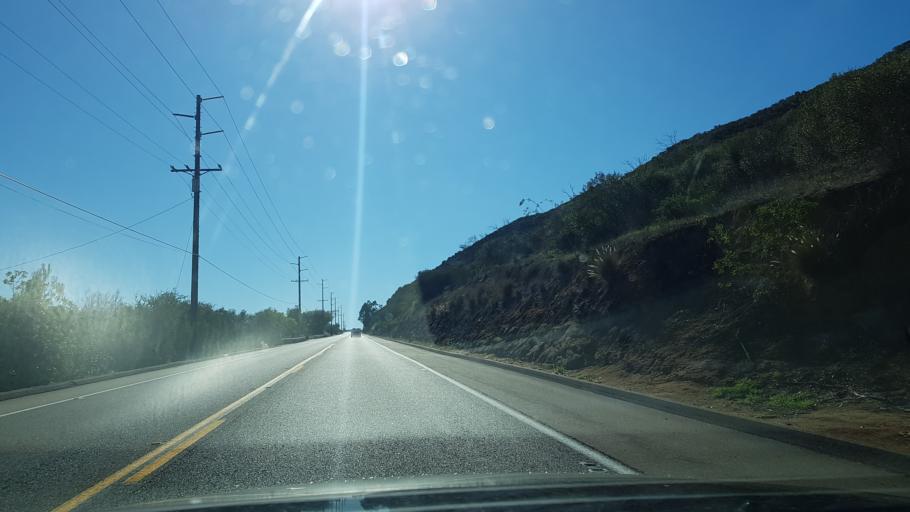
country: US
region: California
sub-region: San Diego County
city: Escondido
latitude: 33.0786
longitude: -117.1206
